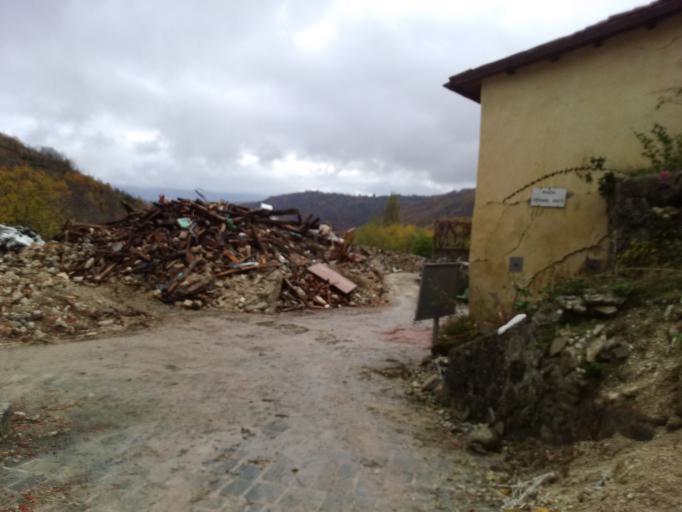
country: IT
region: Latium
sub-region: Provincia di Rieti
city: Accumoli
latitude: 42.6933
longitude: 13.2073
